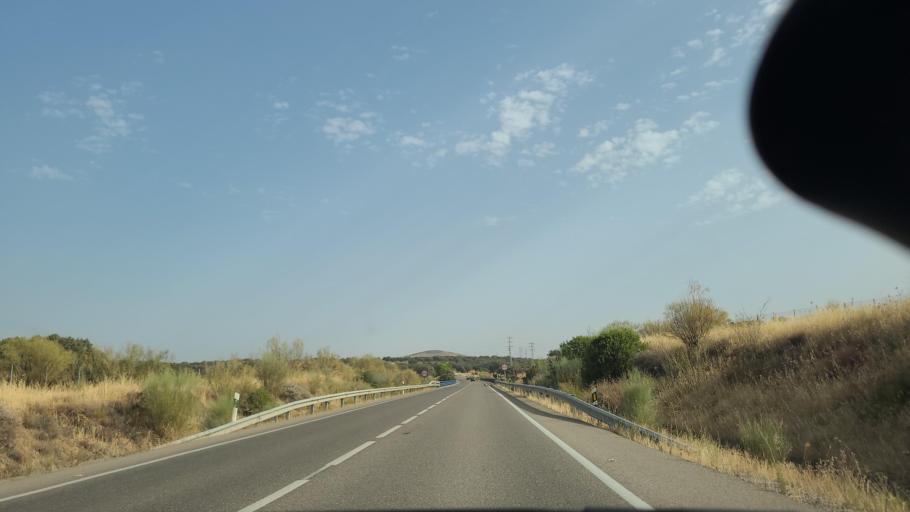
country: ES
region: Andalusia
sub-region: Province of Cordoba
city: Belmez
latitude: 38.2460
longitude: -5.1673
